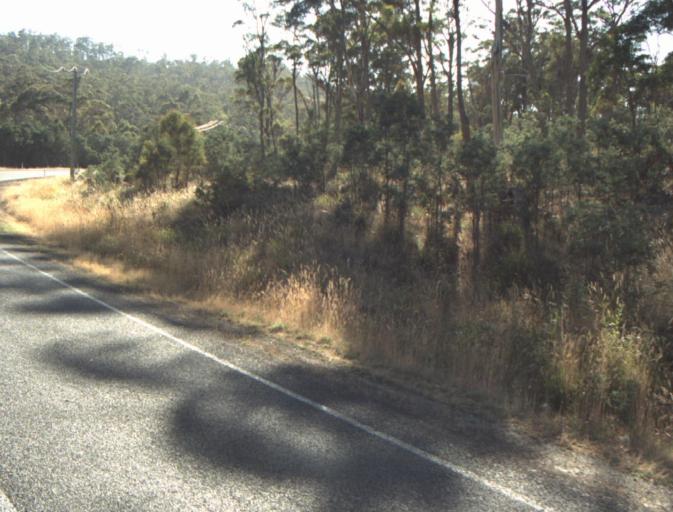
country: AU
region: Tasmania
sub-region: Launceston
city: Newstead
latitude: -41.4183
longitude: 147.2590
